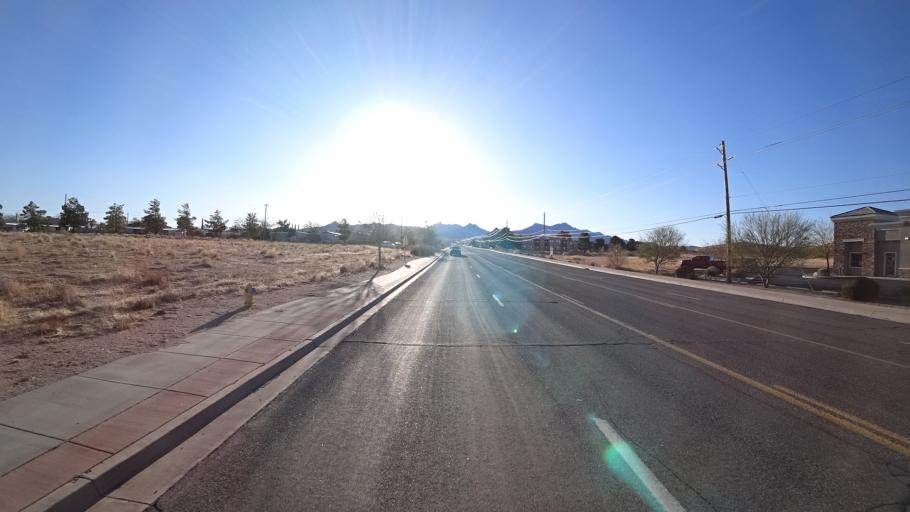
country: US
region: Arizona
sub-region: Mohave County
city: Kingman
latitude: 35.1896
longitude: -114.0127
